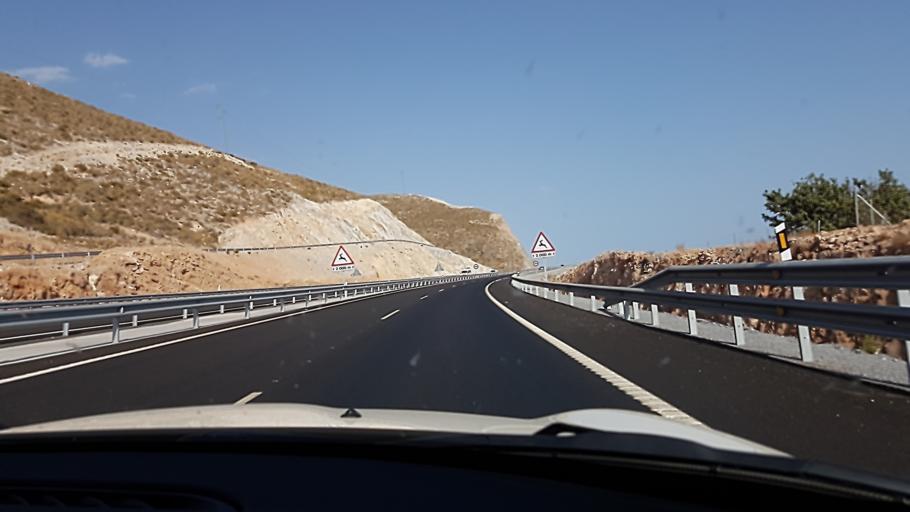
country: ES
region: Andalusia
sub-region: Provincia de Granada
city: Gualchos
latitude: 36.7154
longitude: -3.3940
